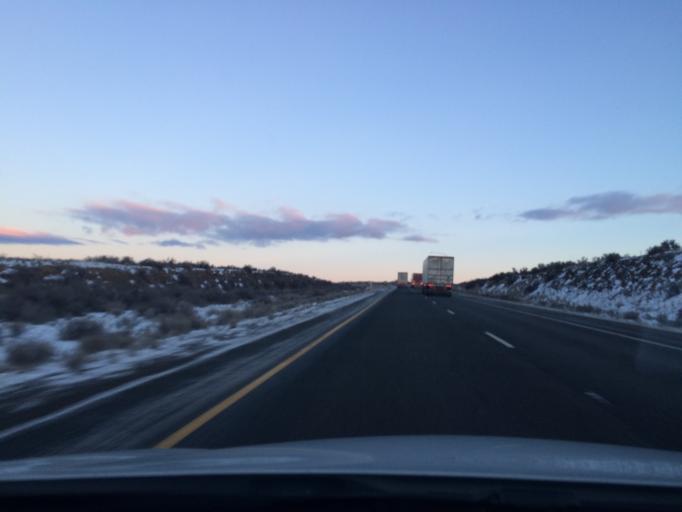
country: US
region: Washington
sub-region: Kittitas County
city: Kittitas
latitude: 46.9424
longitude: -120.2136
